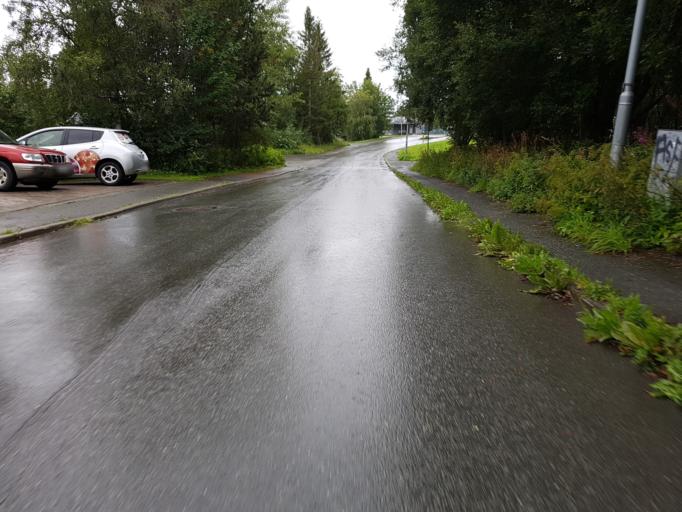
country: NO
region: Sor-Trondelag
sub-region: Trondheim
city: Trondheim
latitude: 63.4046
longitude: 10.4561
